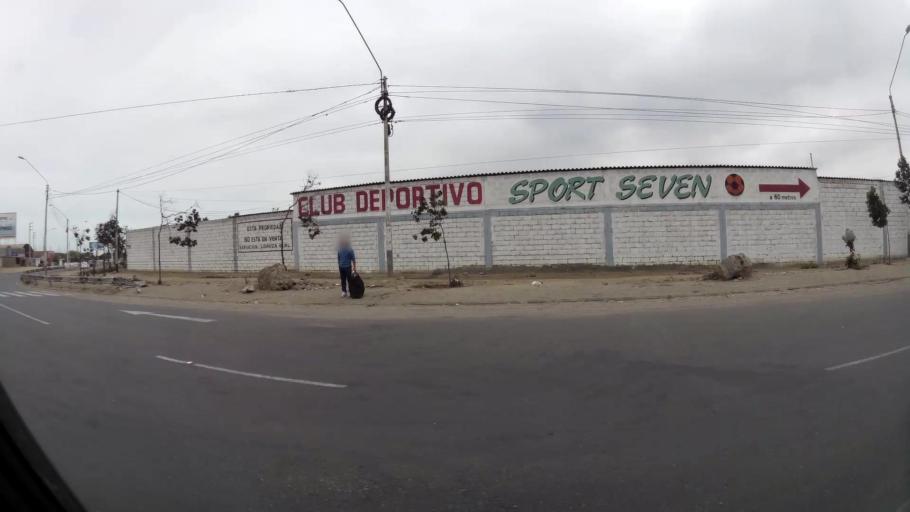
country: PE
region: La Libertad
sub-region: Provincia de Trujillo
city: Huanchaco
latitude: -8.0869
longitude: -79.0967
